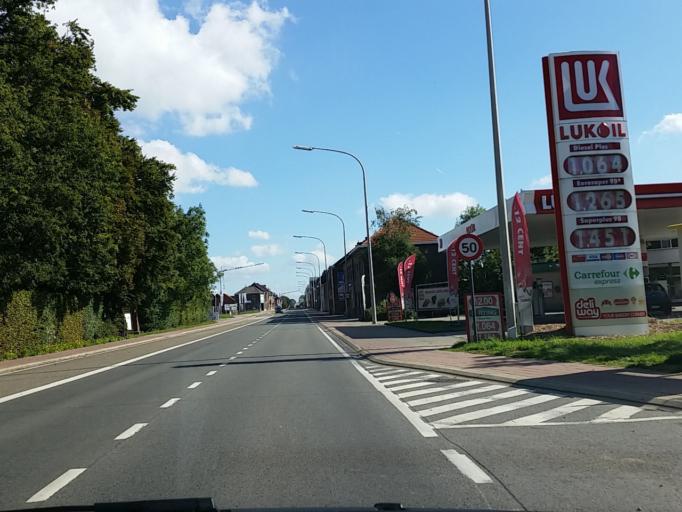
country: BE
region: Flanders
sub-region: Provincie Vlaams-Brabant
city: Holsbeek
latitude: 50.8892
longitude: 4.7649
